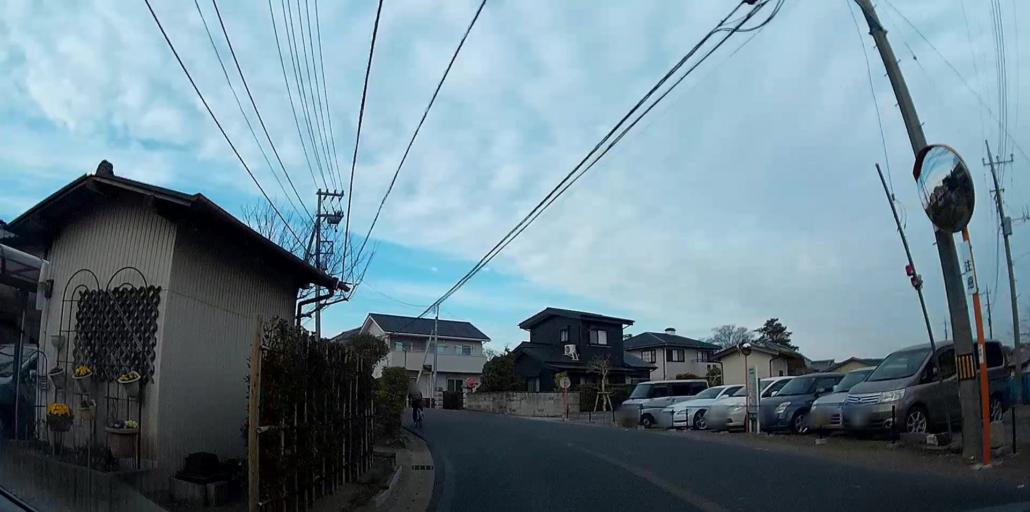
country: JP
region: Chiba
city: Kisarazu
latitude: 35.3685
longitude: 140.0597
